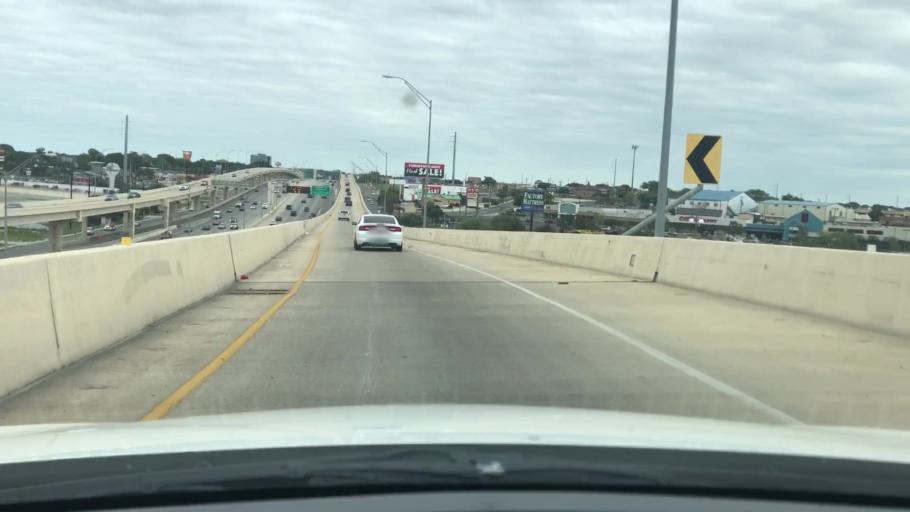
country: US
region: Texas
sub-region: Bexar County
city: Leon Valley
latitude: 29.4830
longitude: -98.5985
